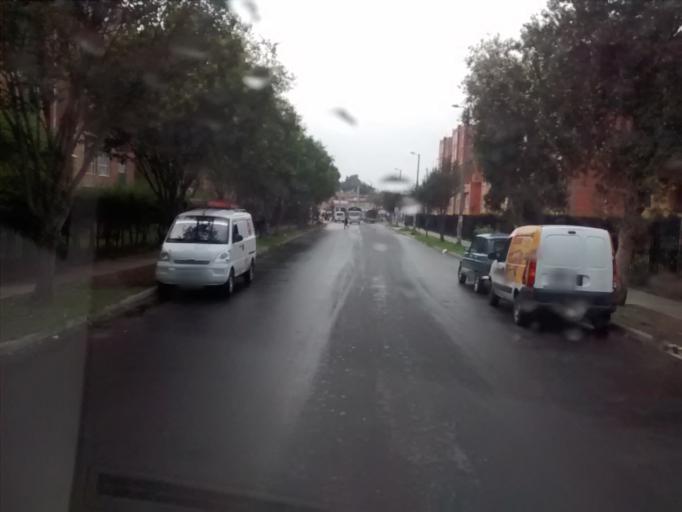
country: CO
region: Cundinamarca
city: Cota
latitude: 4.7568
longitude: -74.1010
